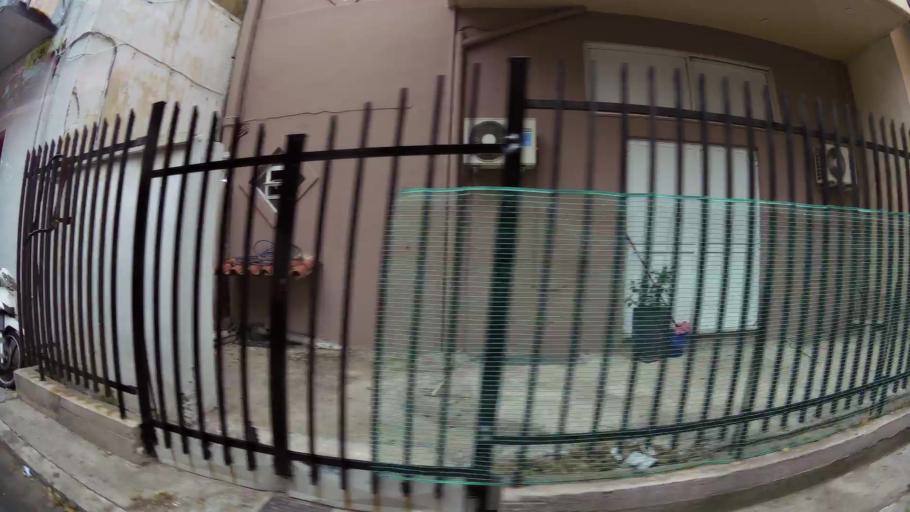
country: GR
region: Attica
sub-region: Nomarchia Athinas
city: Aigaleo
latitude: 37.9850
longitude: 23.6749
